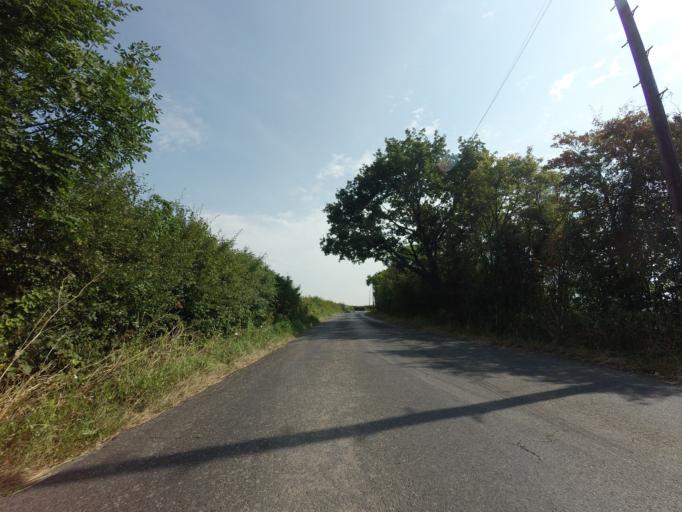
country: GB
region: England
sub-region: Kent
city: Headcorn
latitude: 51.1504
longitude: 0.6017
